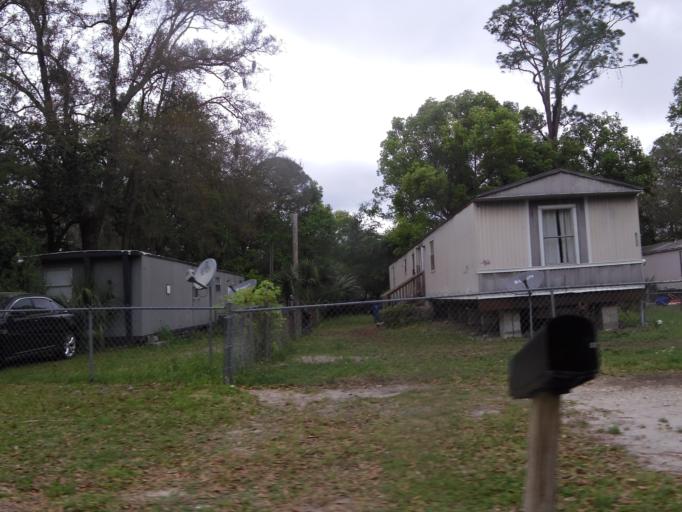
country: US
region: Florida
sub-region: Duval County
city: Jacksonville
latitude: 30.3162
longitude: -81.5632
